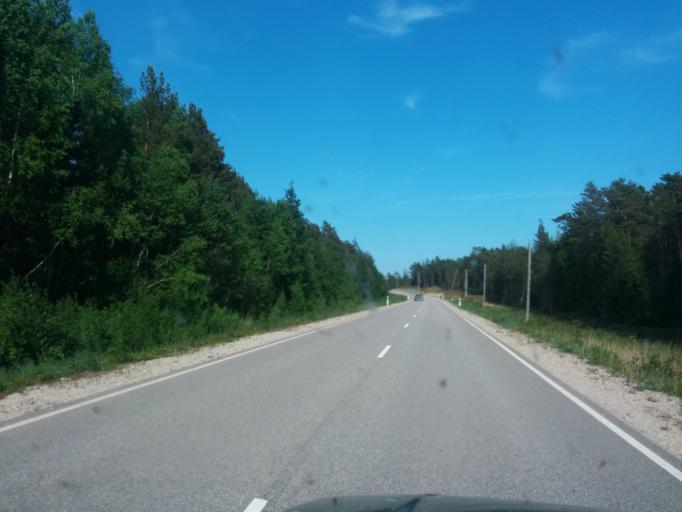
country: LV
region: Dundaga
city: Dundaga
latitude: 57.6703
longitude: 22.3021
